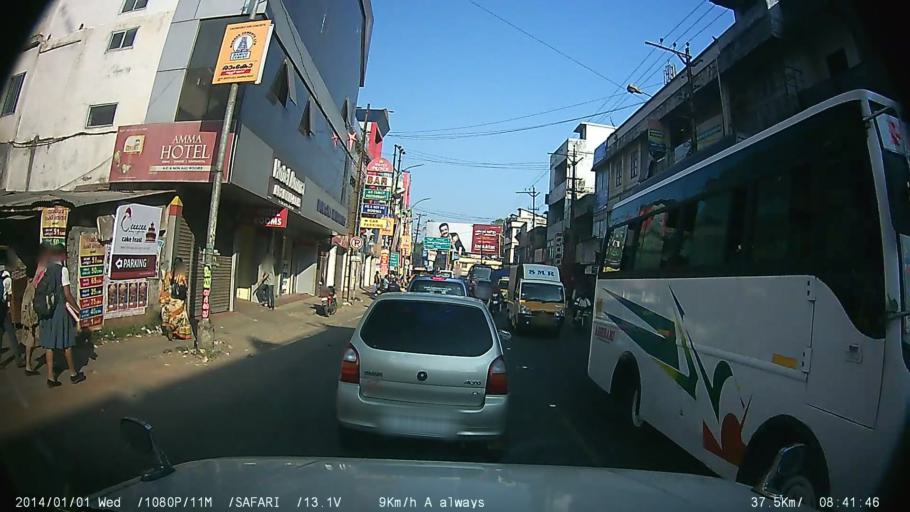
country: IN
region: Kerala
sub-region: Ernakulam
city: Angamali
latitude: 10.1651
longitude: 76.4394
